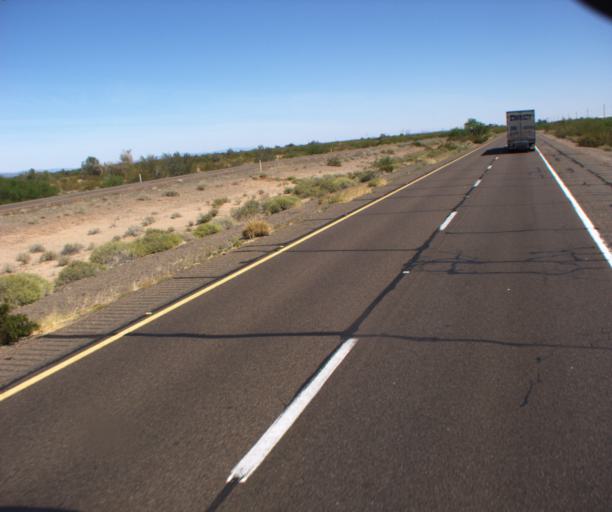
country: US
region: Arizona
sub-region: Yuma County
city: Wellton
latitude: 32.8209
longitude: -113.4697
